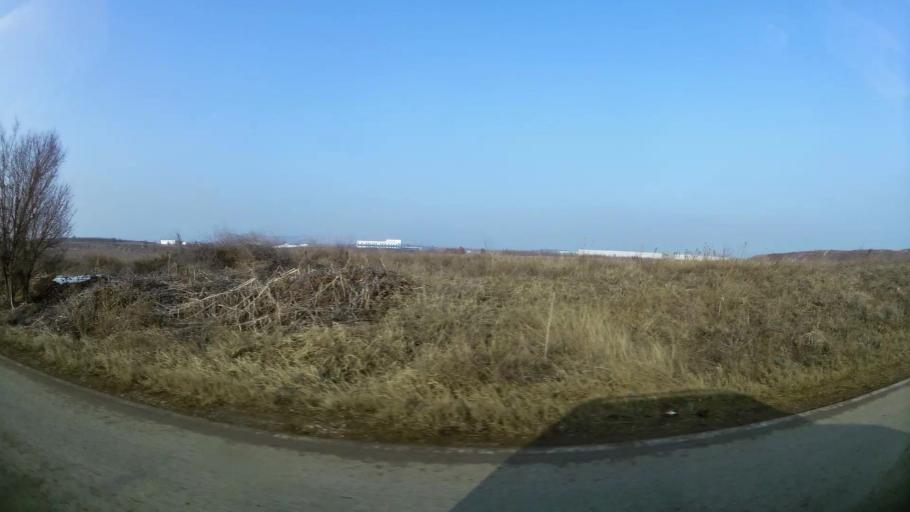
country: MK
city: Kadino
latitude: 41.9780
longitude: 21.6223
